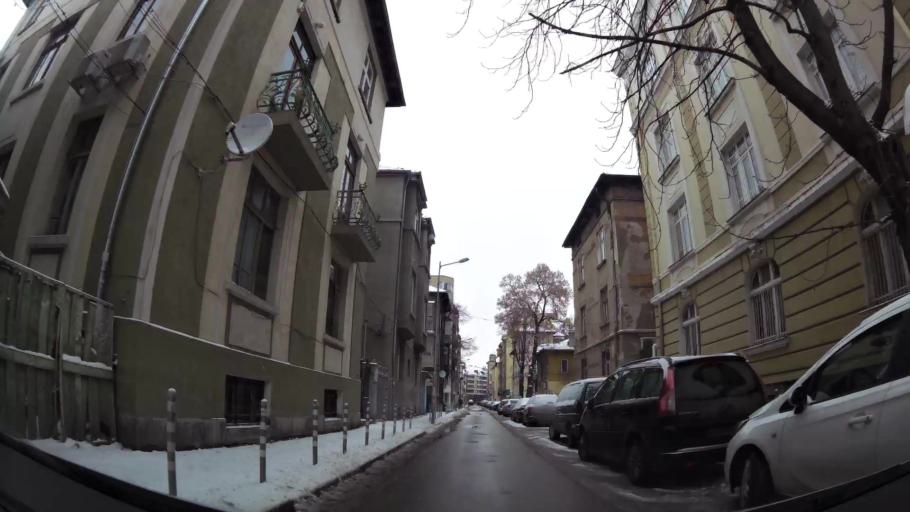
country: BG
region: Sofia-Capital
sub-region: Stolichna Obshtina
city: Sofia
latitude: 42.7010
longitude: 23.3320
